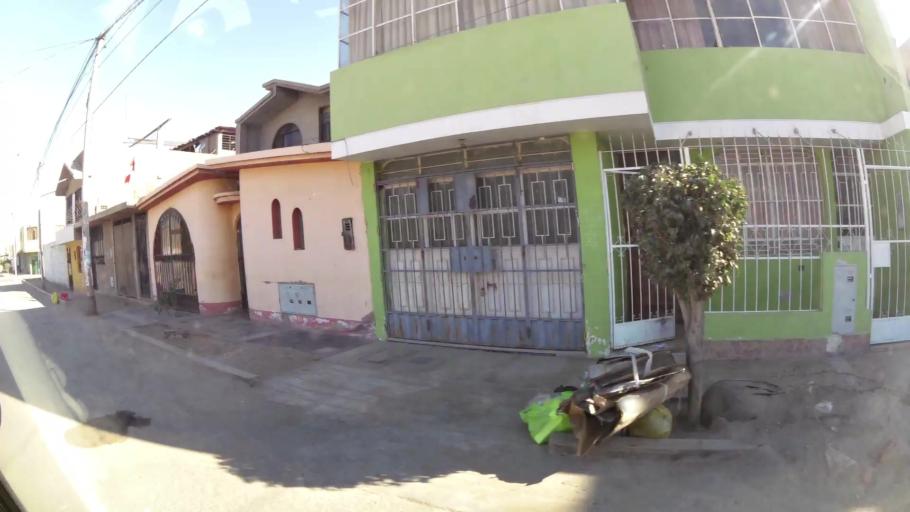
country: PE
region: Ica
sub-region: Provincia de Ica
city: La Tinguina
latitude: -14.0410
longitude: -75.7081
